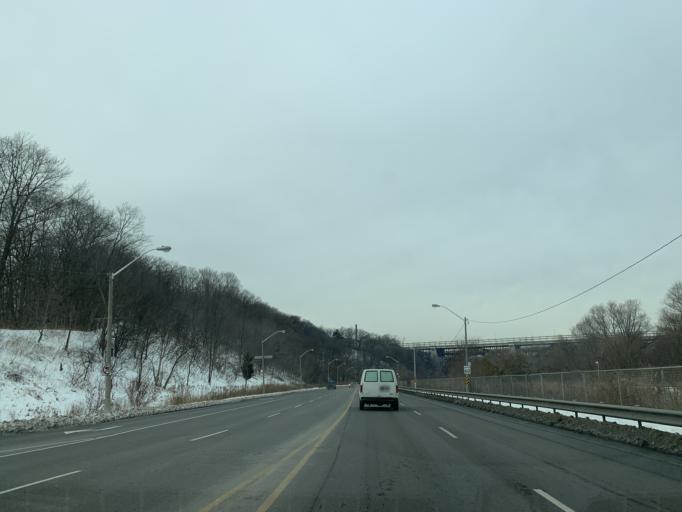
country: CA
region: Ontario
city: Toronto
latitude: 43.6707
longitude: -79.3608
